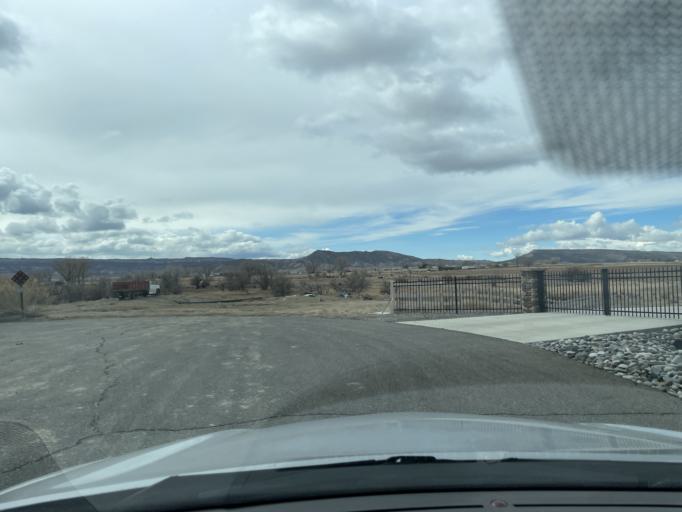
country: US
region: Colorado
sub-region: Mesa County
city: Loma
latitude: 39.2151
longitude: -108.8053
